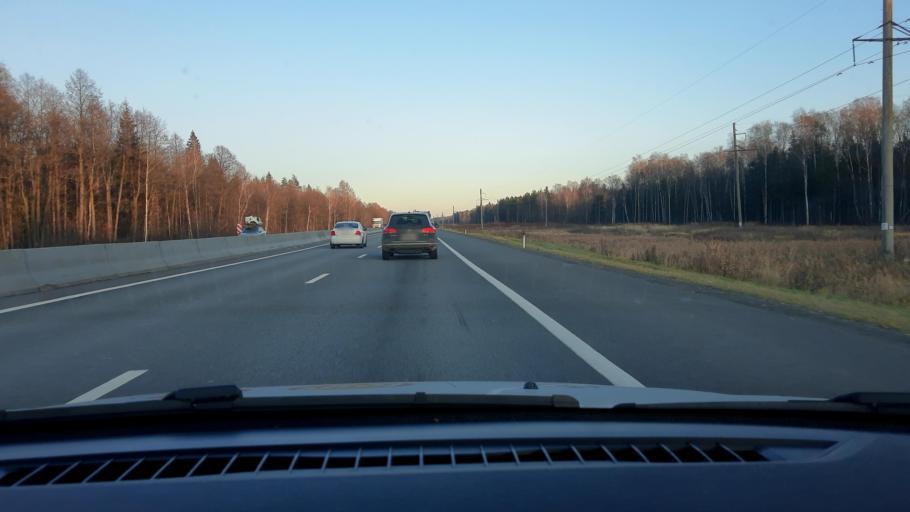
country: RU
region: Nizjnij Novgorod
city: Smolino
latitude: 56.2843
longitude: 43.1456
